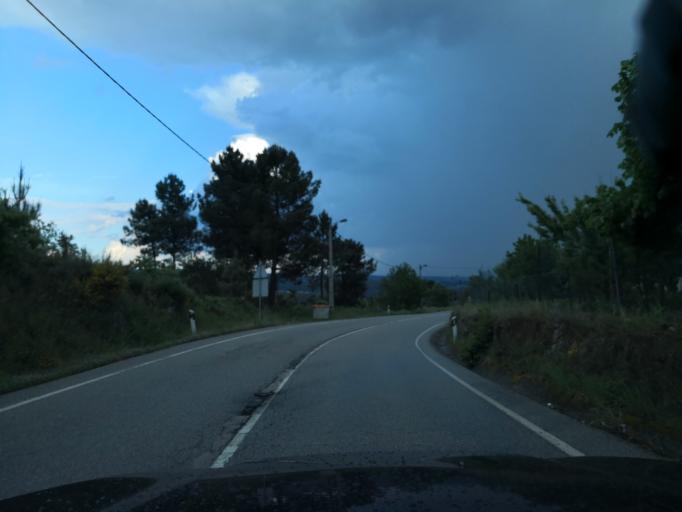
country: PT
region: Vila Real
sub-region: Vila Real
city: Vila Real
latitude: 41.3746
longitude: -7.7167
